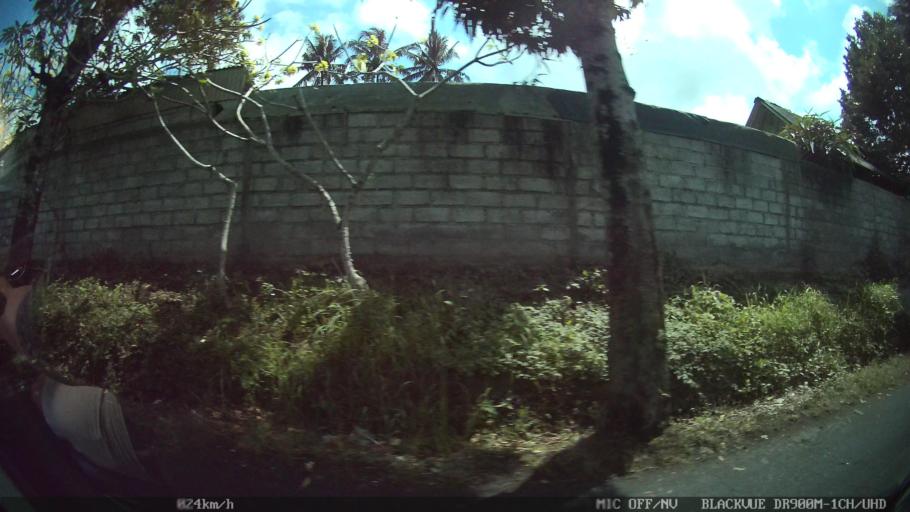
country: ID
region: Bali
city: Banjar Sedang
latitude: -8.5616
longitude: 115.2712
